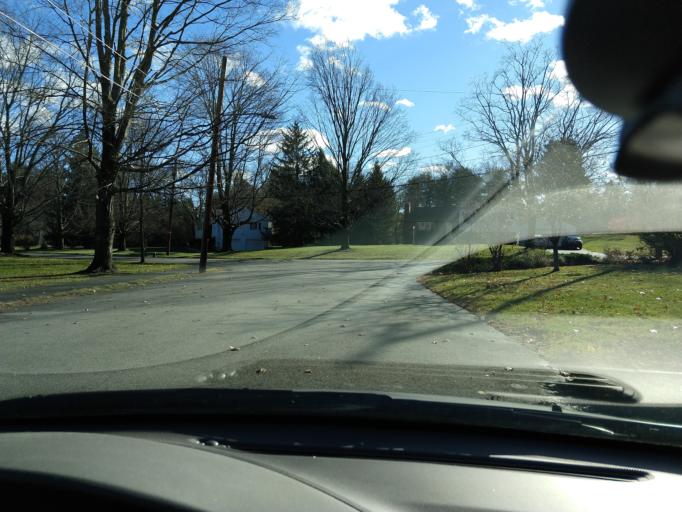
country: US
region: Massachusetts
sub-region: Middlesex County
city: Bedford
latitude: 42.5037
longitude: -71.2590
